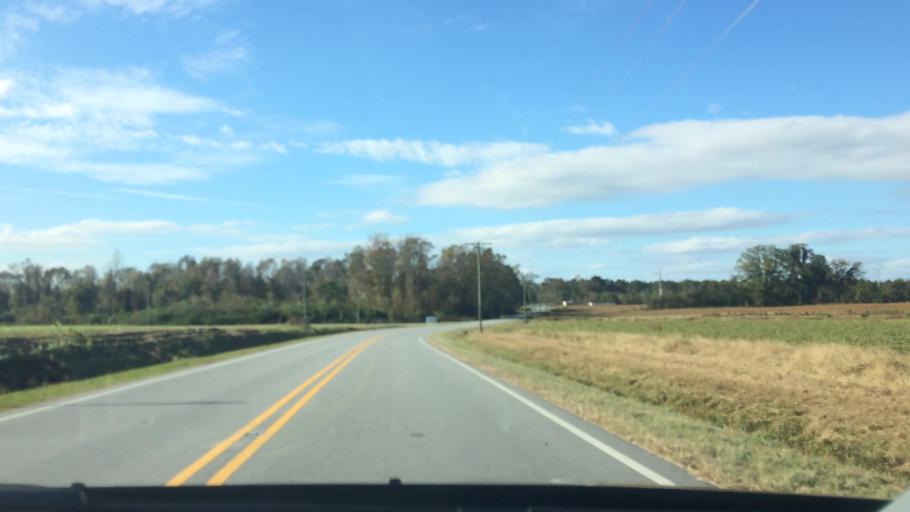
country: US
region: North Carolina
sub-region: Greene County
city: Maury
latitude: 35.4742
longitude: -77.6191
